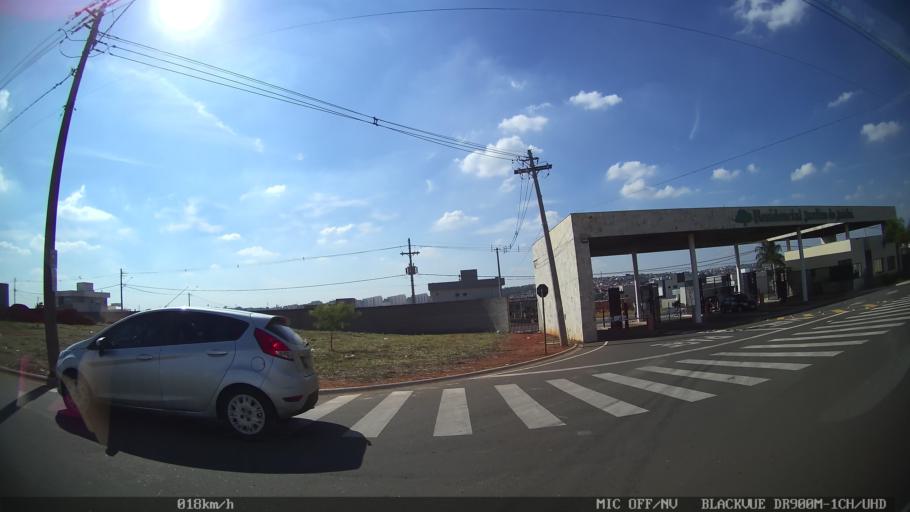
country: BR
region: Sao Paulo
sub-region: Hortolandia
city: Hortolandia
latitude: -22.8656
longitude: -47.2304
